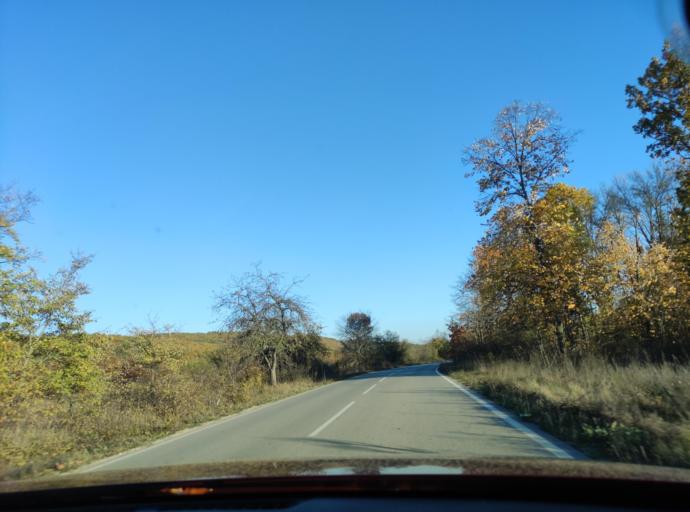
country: BG
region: Montana
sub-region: Obshtina Chiprovtsi
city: Chiprovtsi
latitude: 43.4192
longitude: 23.0234
